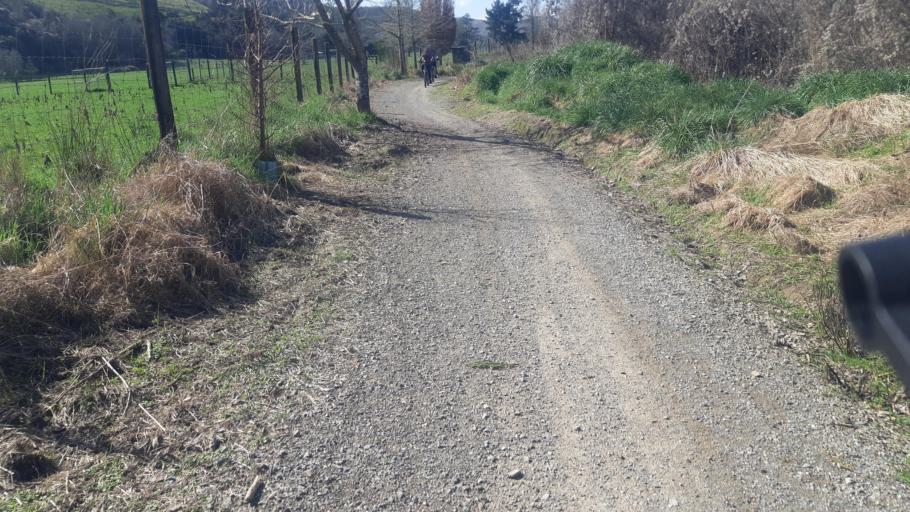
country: NZ
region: Tasman
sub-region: Tasman District
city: Wakefield
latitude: -41.4131
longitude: 173.0061
